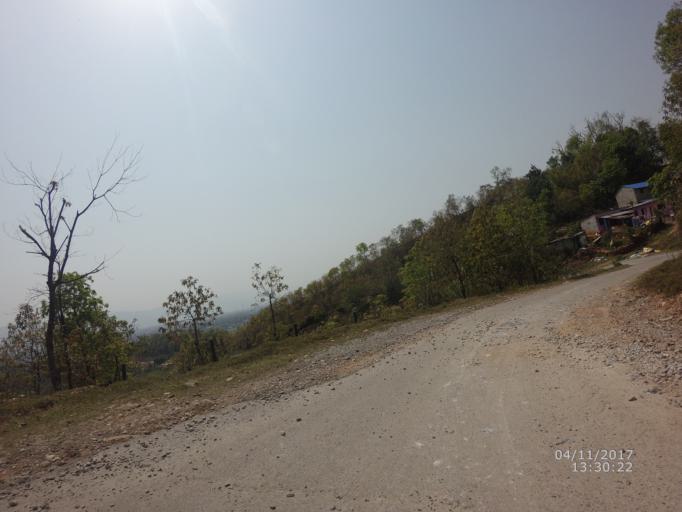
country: NP
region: Western Region
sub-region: Gandaki Zone
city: Pokhara
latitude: 28.1959
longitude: 84.0407
